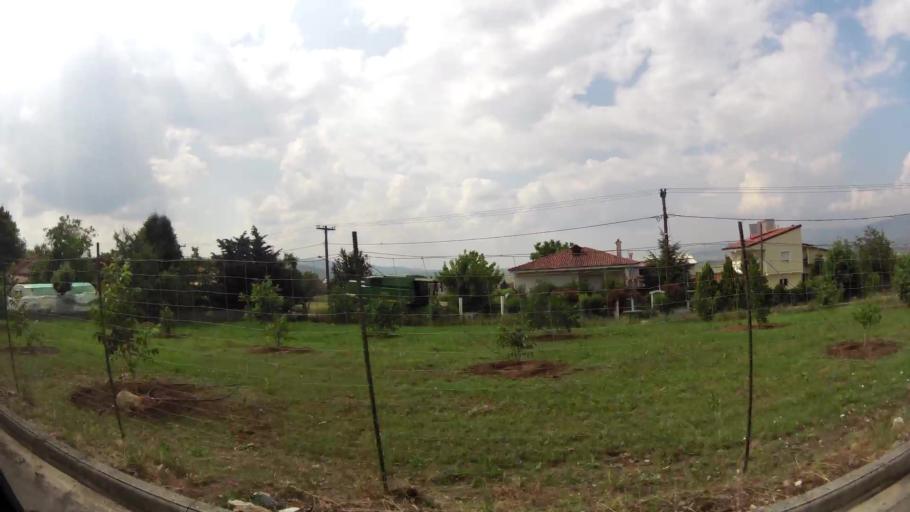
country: GR
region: West Macedonia
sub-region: Nomos Kozanis
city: Koila
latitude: 40.3491
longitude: 21.8418
